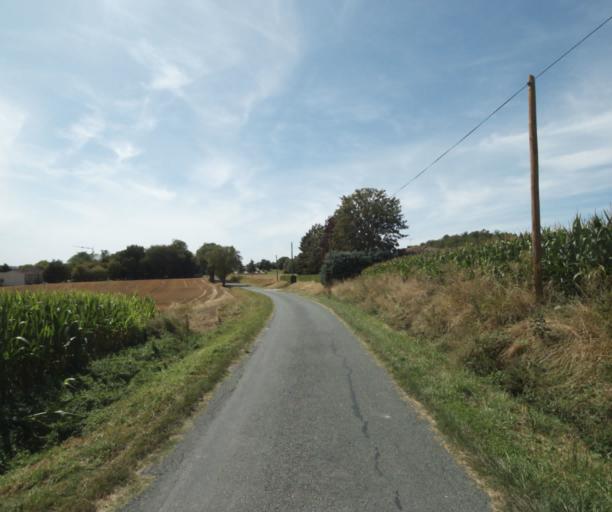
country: FR
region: Midi-Pyrenees
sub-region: Departement du Tarn
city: Puylaurens
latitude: 43.5260
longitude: 2.0135
